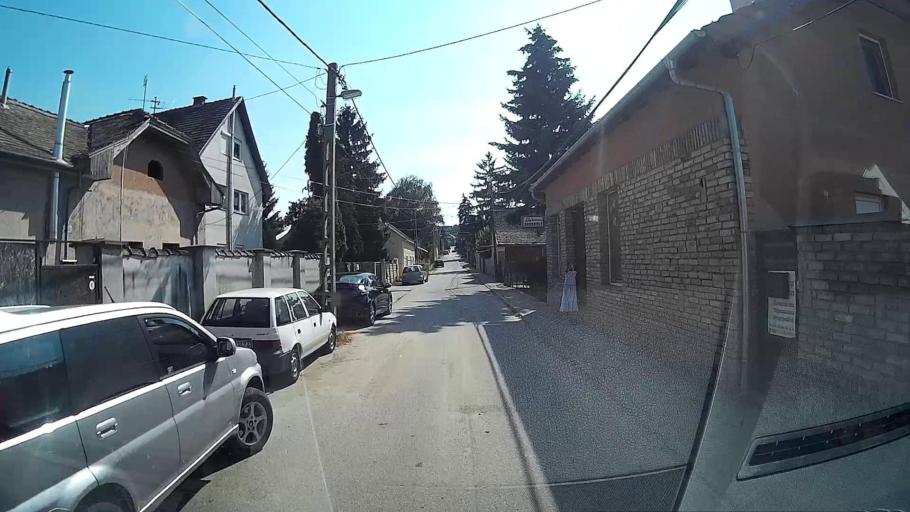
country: HU
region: Pest
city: Pomaz
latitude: 47.6450
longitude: 19.0265
